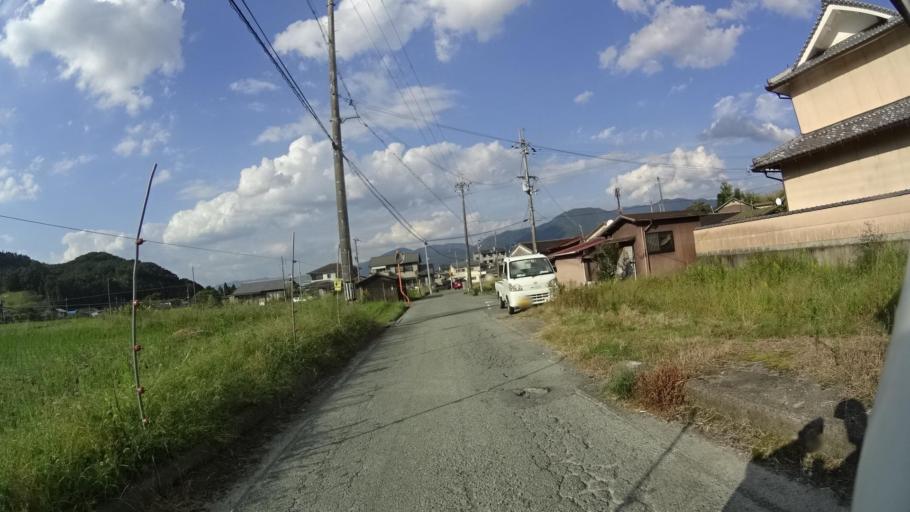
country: JP
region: Kyoto
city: Kameoka
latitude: 35.0051
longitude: 135.5746
